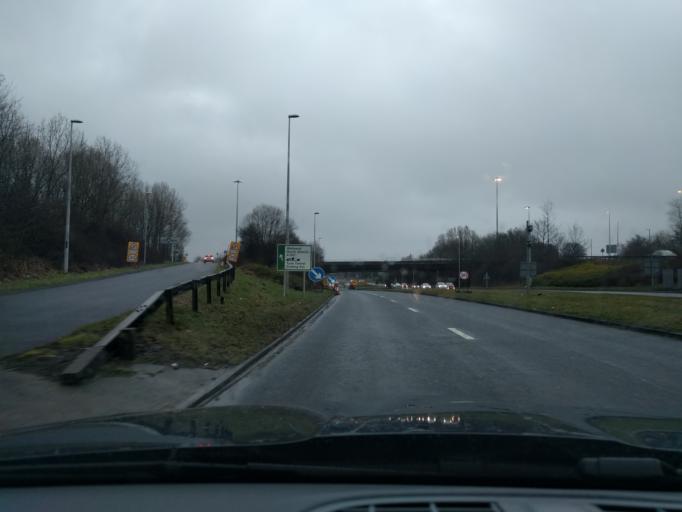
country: GB
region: England
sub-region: South Tyneside
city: Jarrow
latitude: 54.9981
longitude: -1.4853
